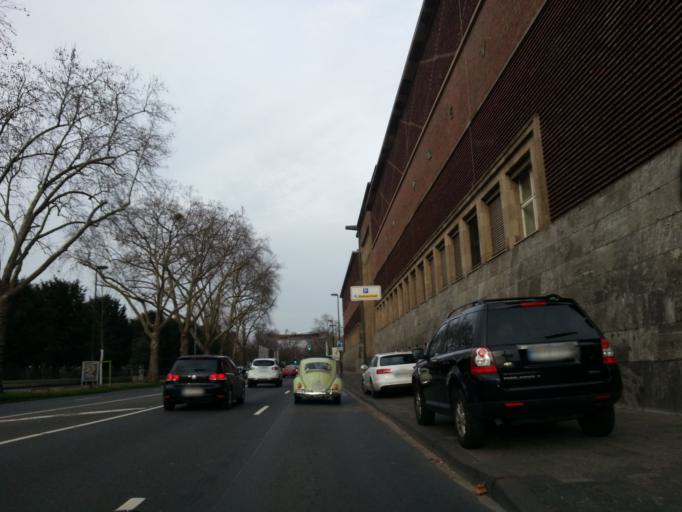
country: DE
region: North Rhine-Westphalia
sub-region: Regierungsbezirk Dusseldorf
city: Dusseldorf
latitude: 51.2343
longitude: 6.7718
